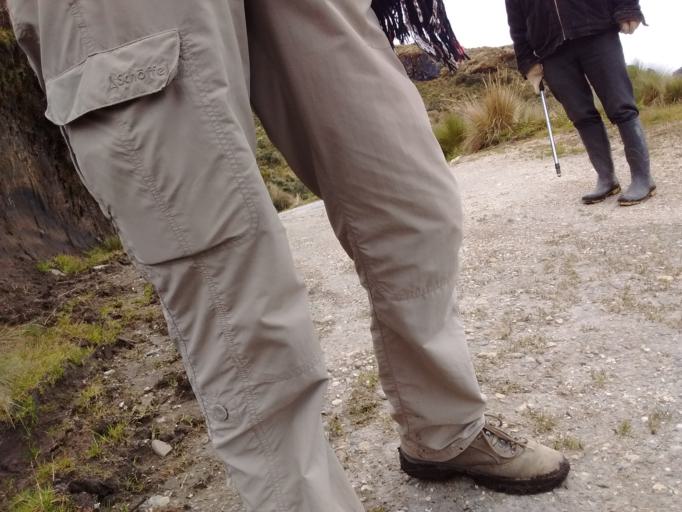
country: CO
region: Cauca
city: Totoro
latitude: 2.3337
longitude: -76.3940
